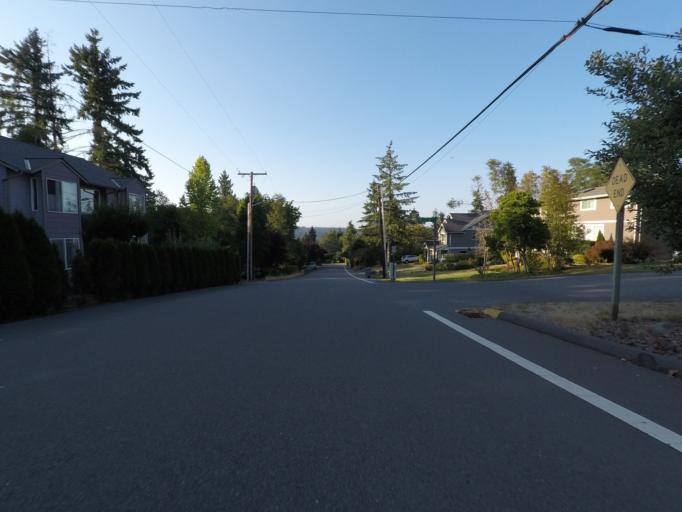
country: US
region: Washington
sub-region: King County
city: Kenmore
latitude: 47.7420
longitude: -122.2327
